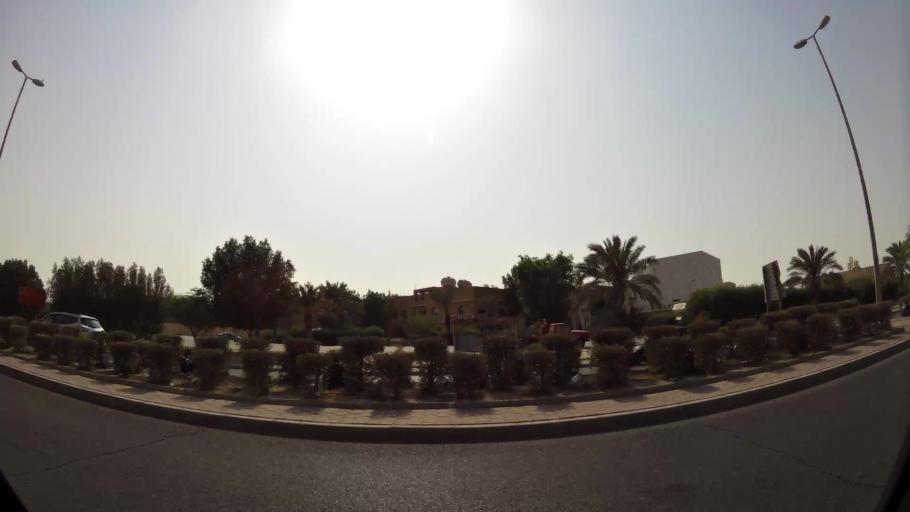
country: KW
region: Muhafazat al Jahra'
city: Al Jahra'
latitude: 29.3449
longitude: 47.6644
